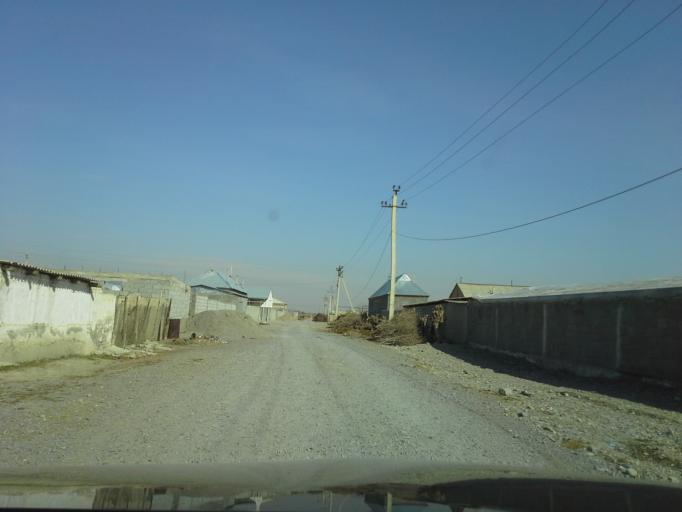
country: TM
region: Ahal
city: Abadan
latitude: 38.1107
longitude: 58.0360
